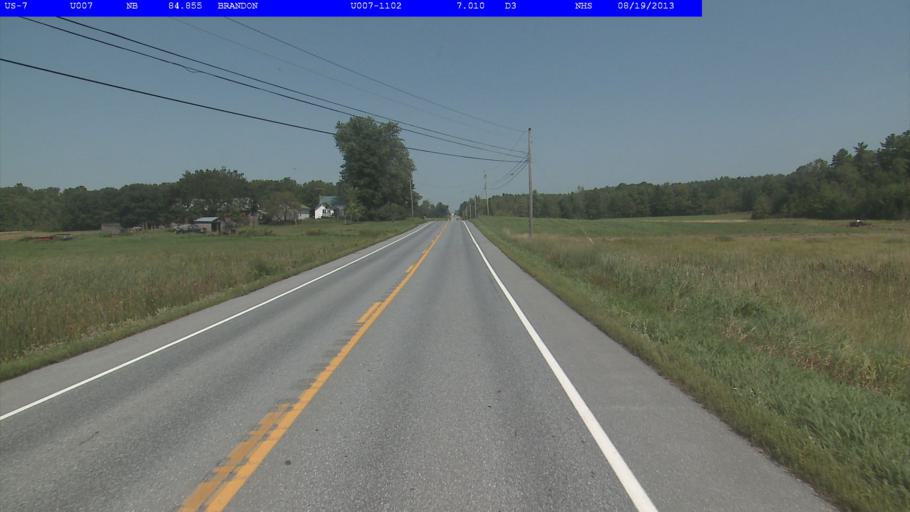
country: US
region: Vermont
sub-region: Rutland County
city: Brandon
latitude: 43.8372
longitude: -73.1061
